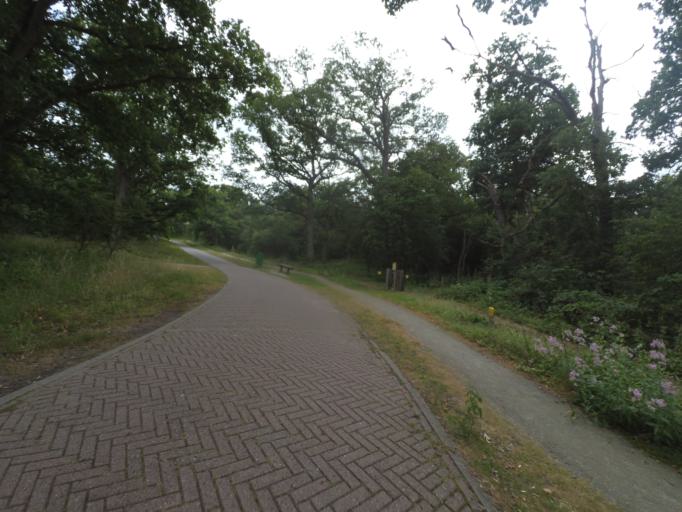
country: NL
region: South Holland
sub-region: Gemeente Den Haag
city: Scheveningen
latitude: 52.1269
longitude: 4.3305
